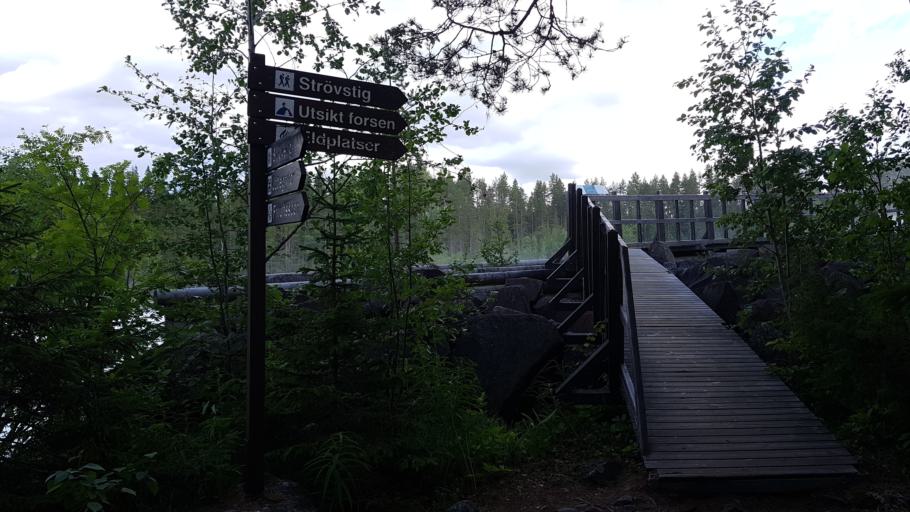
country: SE
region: Norrbotten
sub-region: Alvsbyns Kommun
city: AElvsbyn
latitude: 65.8521
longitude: 20.4092
